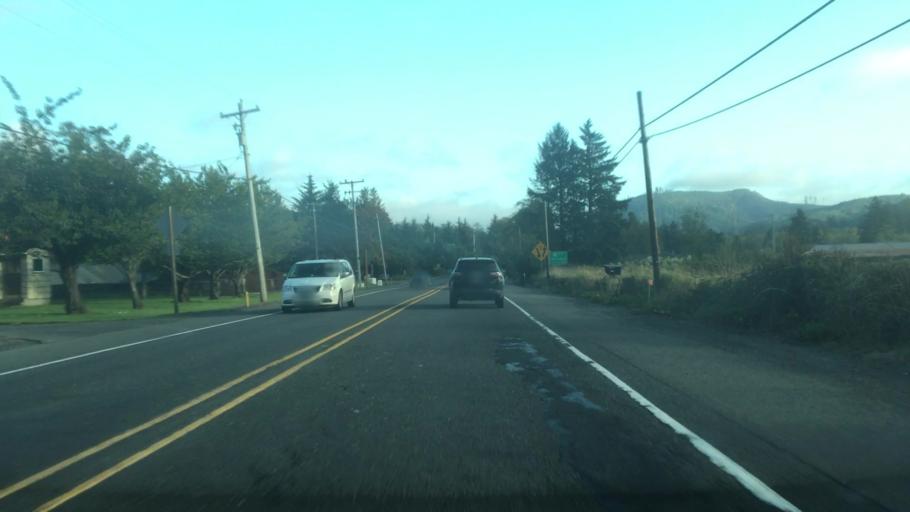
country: US
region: Oregon
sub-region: Clatsop County
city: Seaside
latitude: 45.9495
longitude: -123.9258
